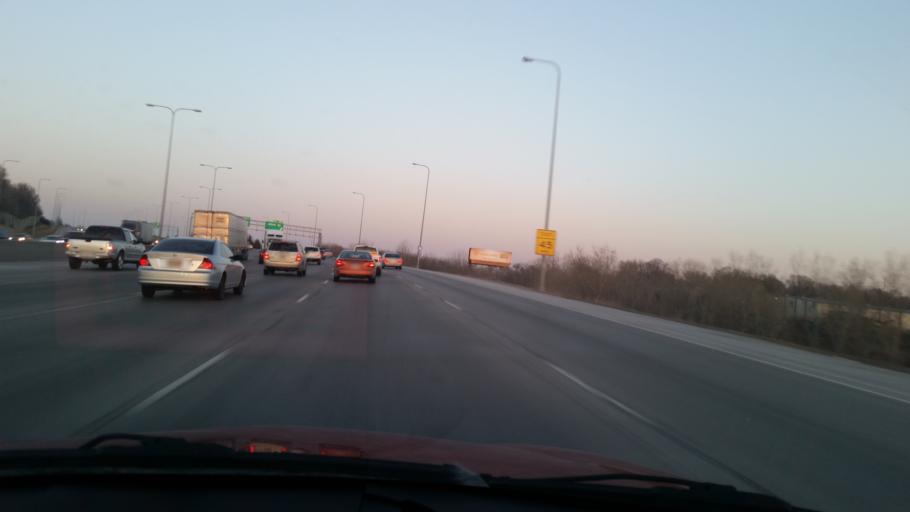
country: US
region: Nebraska
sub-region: Douglas County
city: Omaha
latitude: 41.2224
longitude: -95.9844
